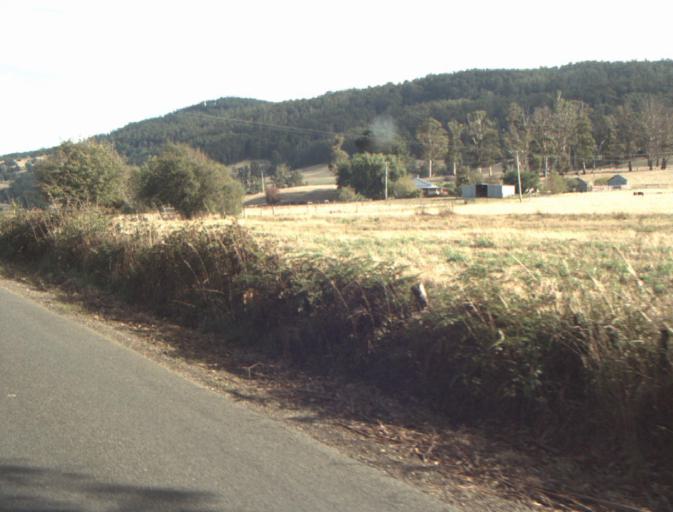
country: AU
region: Tasmania
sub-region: Launceston
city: Mayfield
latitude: -41.2277
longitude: 147.1229
